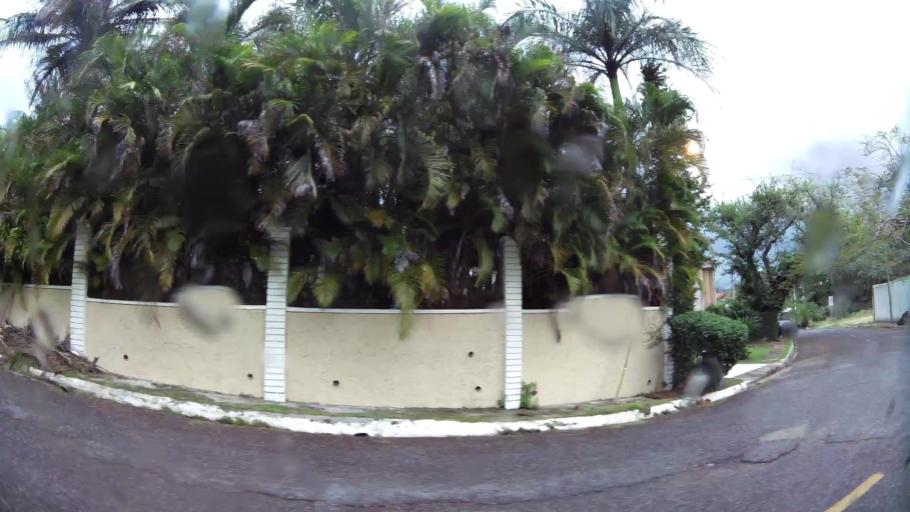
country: DO
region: Nacional
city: La Agustina
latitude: 18.5131
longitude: -69.9339
